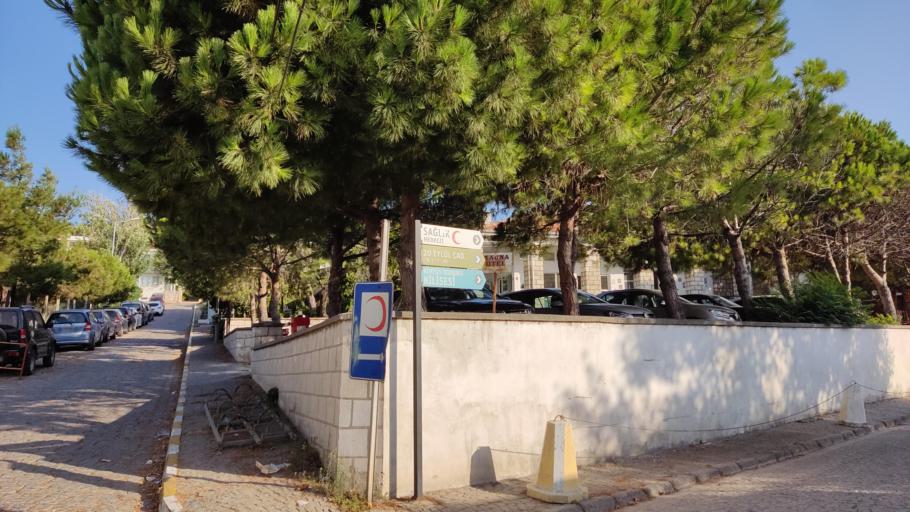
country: TR
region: Canakkale
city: Bozcaada
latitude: 39.8332
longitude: 26.0679
